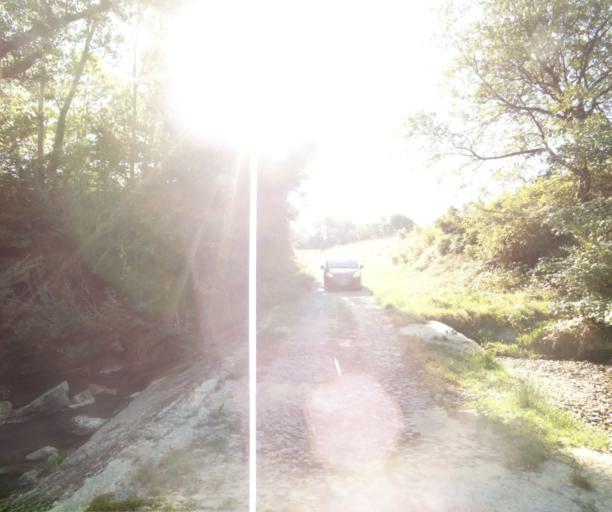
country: FR
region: Midi-Pyrenees
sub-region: Departement du Tarn-et-Garonne
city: Verdun-sur-Garonne
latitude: 43.8642
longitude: 1.2220
